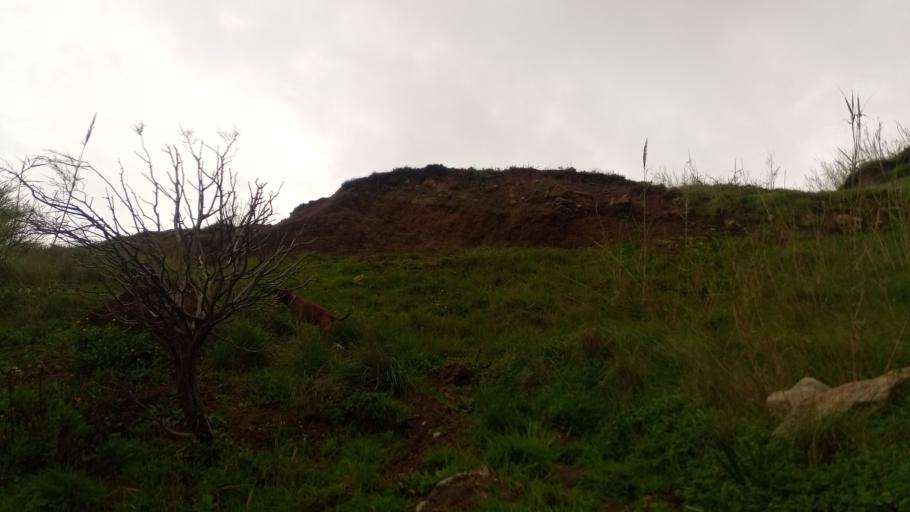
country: PT
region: Leiria
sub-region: Caldas da Rainha
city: Caldas da Rainha
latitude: 39.4715
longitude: -9.2000
